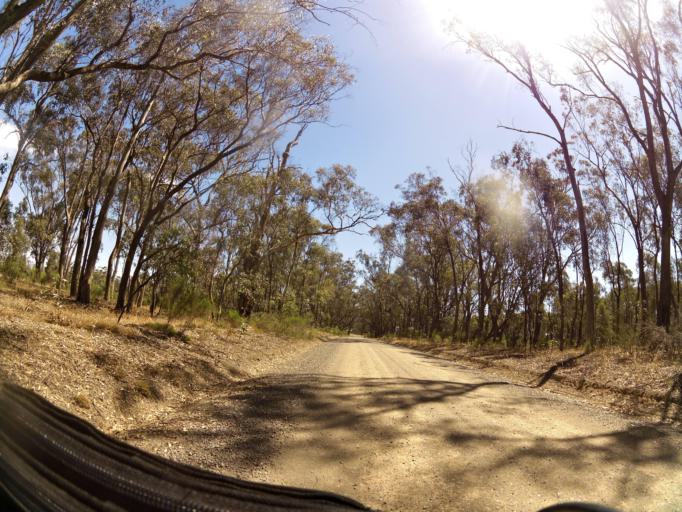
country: AU
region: Victoria
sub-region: Campaspe
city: Kyabram
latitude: -36.8414
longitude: 145.0695
